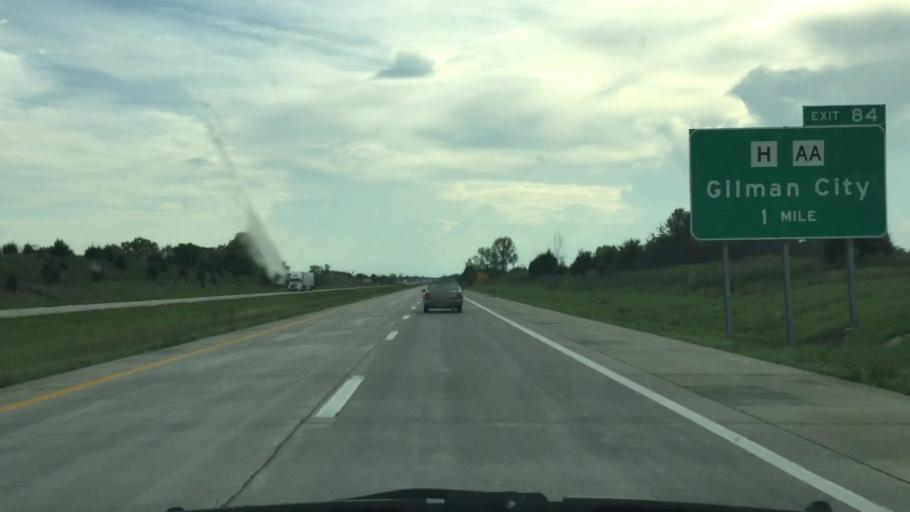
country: US
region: Missouri
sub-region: Harrison County
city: Bethany
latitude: 40.1698
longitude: -94.0231
